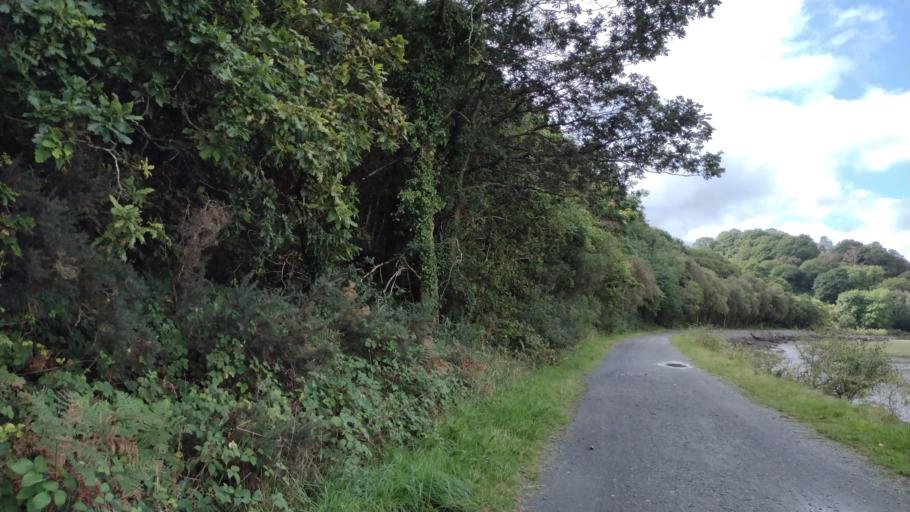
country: GB
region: Wales
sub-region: Gwynedd
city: Barmouth
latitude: 52.7231
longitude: -3.9999
